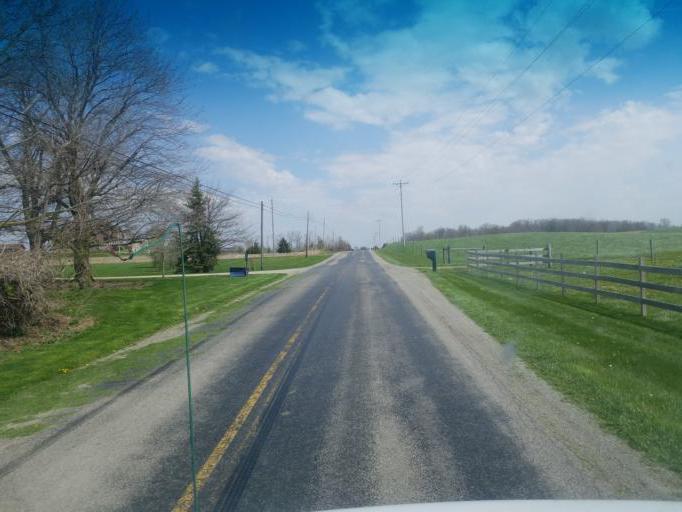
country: US
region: Ohio
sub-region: Hardin County
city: Kenton
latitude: 40.5926
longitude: -83.6738
